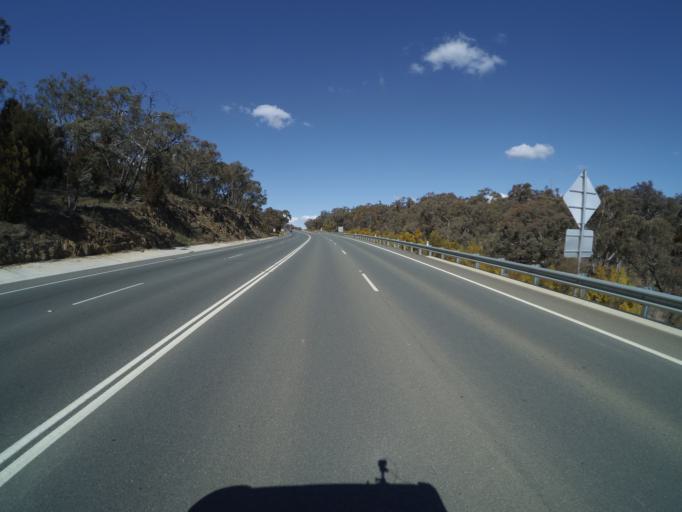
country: AU
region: New South Wales
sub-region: Queanbeyan
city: Queanbeyan
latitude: -35.3412
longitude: 149.2601
